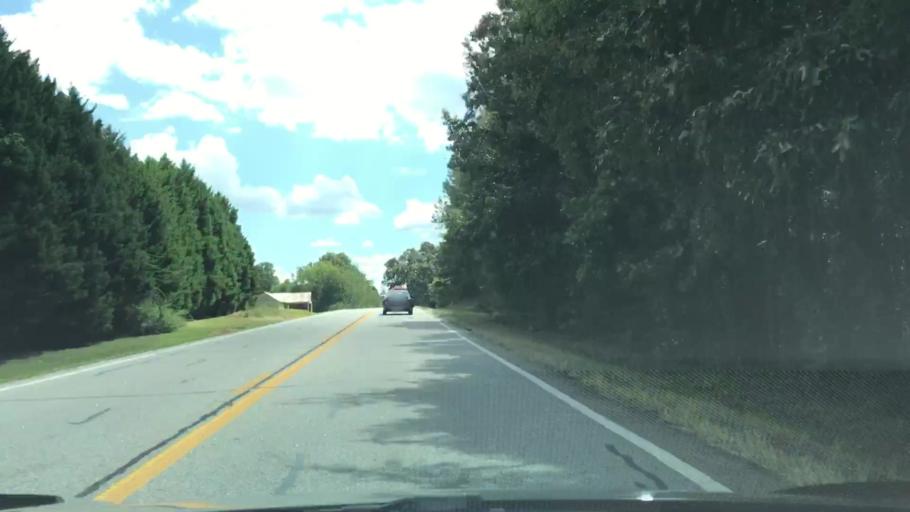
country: US
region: Georgia
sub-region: Oconee County
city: Watkinsville
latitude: 33.7764
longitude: -83.3110
